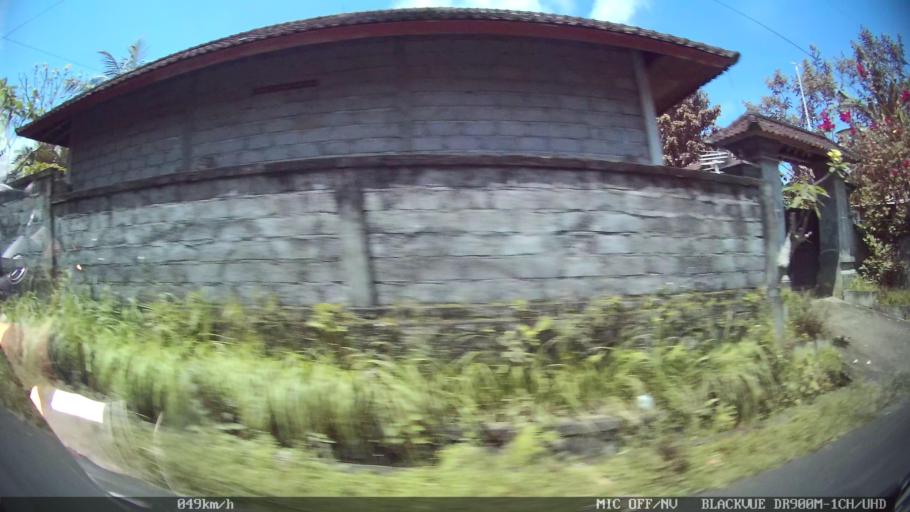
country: ID
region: Bali
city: Banjar Kelodan
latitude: -8.5248
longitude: 115.3339
